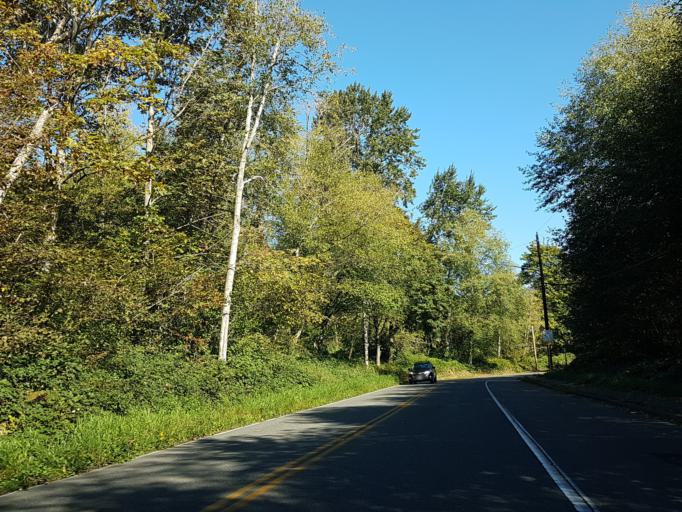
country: US
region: Washington
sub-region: Snohomish County
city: Brier
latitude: 47.7776
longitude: -122.2604
